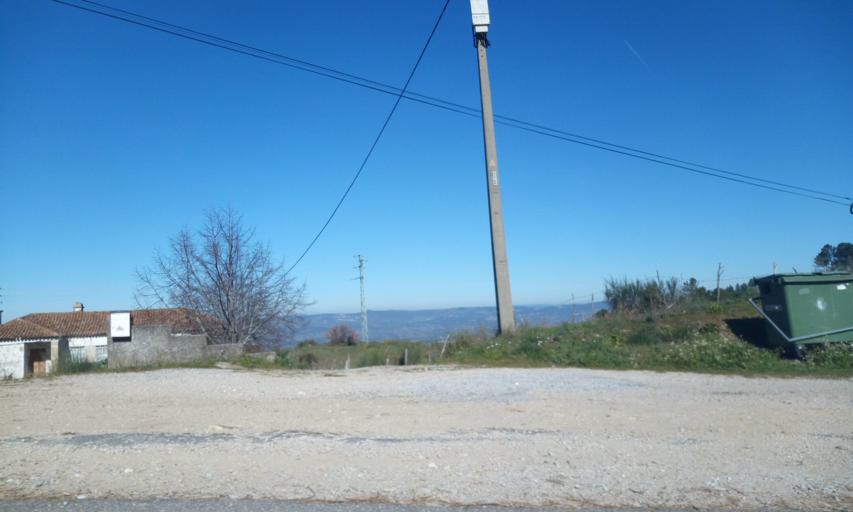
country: PT
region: Guarda
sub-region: Manteigas
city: Manteigas
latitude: 40.5109
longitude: -7.5652
